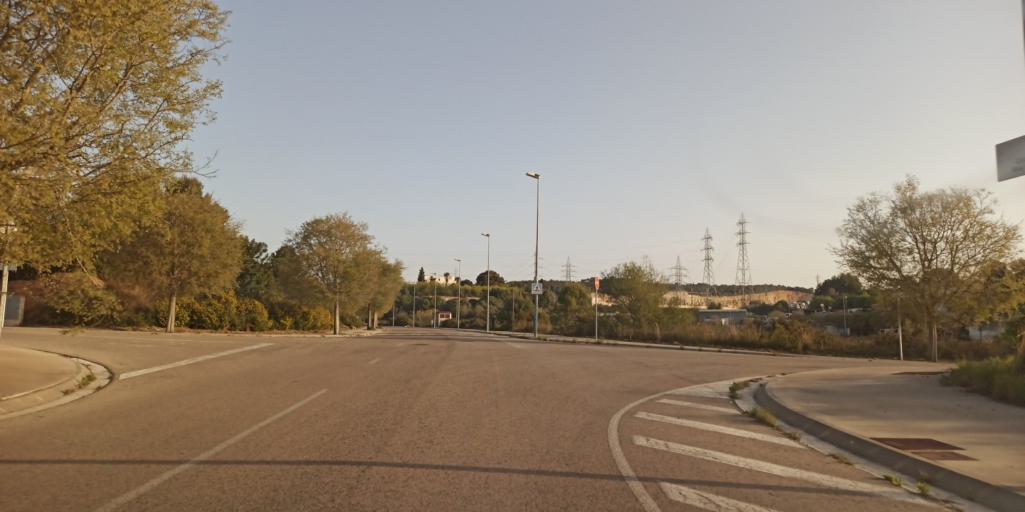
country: ES
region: Catalonia
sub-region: Provincia de Barcelona
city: Vilanova i la Geltru
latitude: 41.2490
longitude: 1.7211
